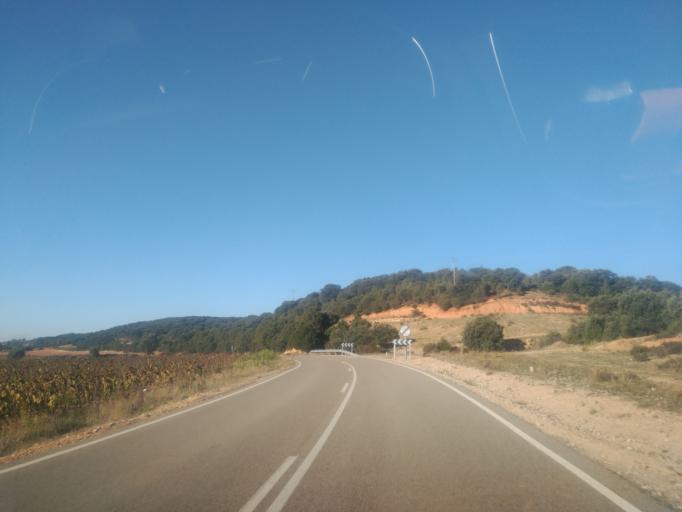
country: ES
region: Castille and Leon
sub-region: Provincia de Soria
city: Alcubilla de Avellaneda
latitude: 41.7431
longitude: -3.2895
